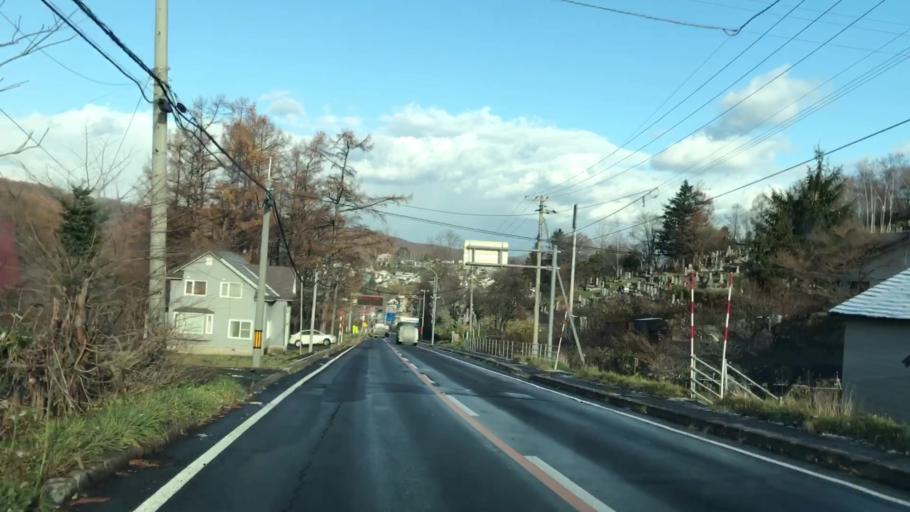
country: JP
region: Hokkaido
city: Otaru
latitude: 43.1641
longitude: 140.9971
